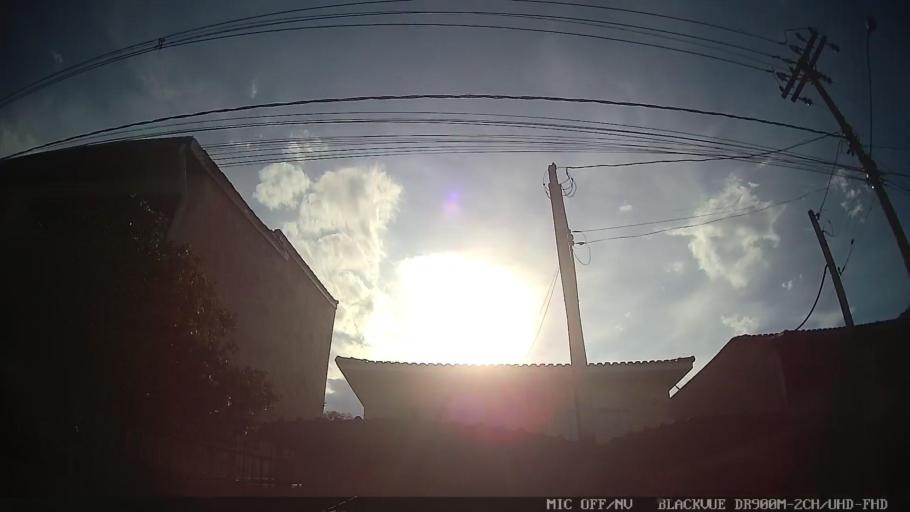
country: BR
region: Sao Paulo
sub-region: Amparo
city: Amparo
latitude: -22.6897
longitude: -46.6907
